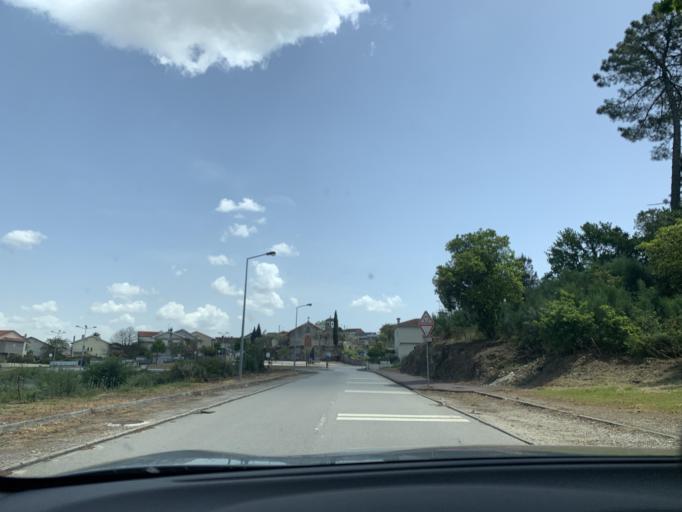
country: PT
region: Viseu
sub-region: Mangualde
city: Mangualde
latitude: 40.6085
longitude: -7.7685
